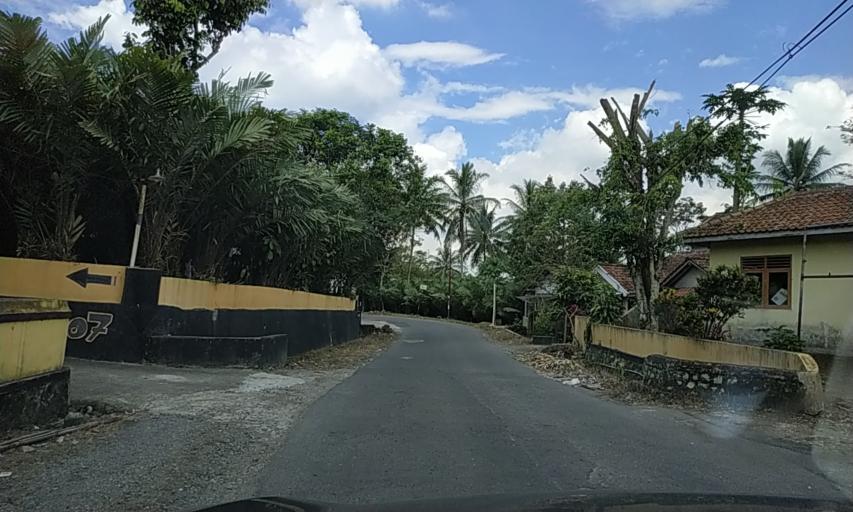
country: ID
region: Daerah Istimewa Yogyakarta
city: Sleman
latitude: -7.6323
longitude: 110.4008
